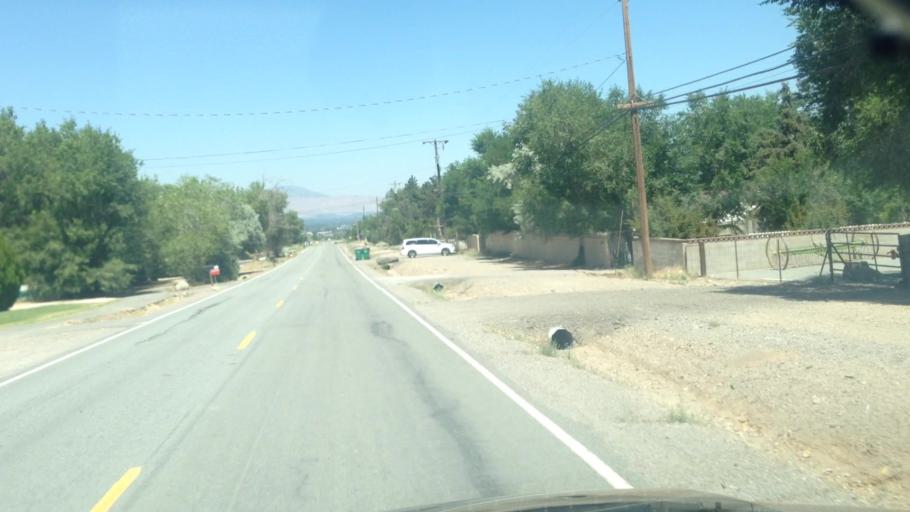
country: US
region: Nevada
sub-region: Storey County
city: Virginia City
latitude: 39.3828
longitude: -119.7229
